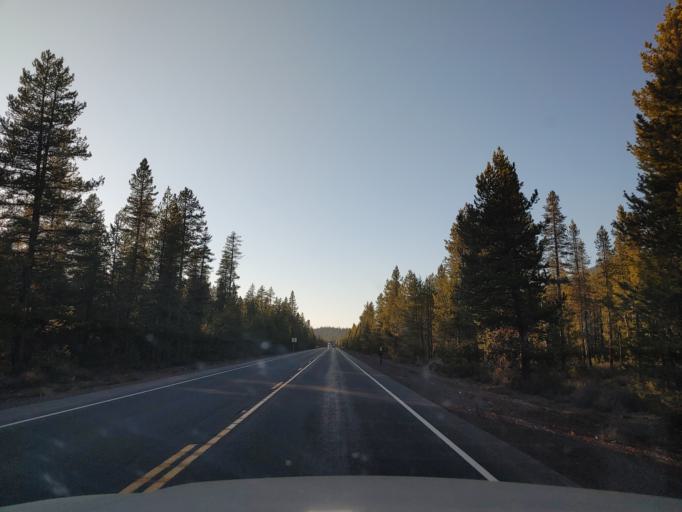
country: US
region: Oregon
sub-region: Deschutes County
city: La Pine
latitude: 43.4308
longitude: -121.8535
